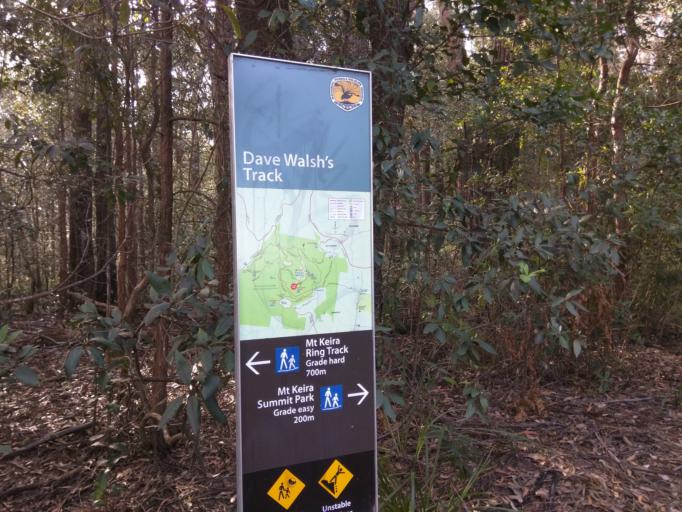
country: AU
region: New South Wales
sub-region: Wollongong
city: Mount Keira
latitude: -34.4040
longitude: 150.8546
